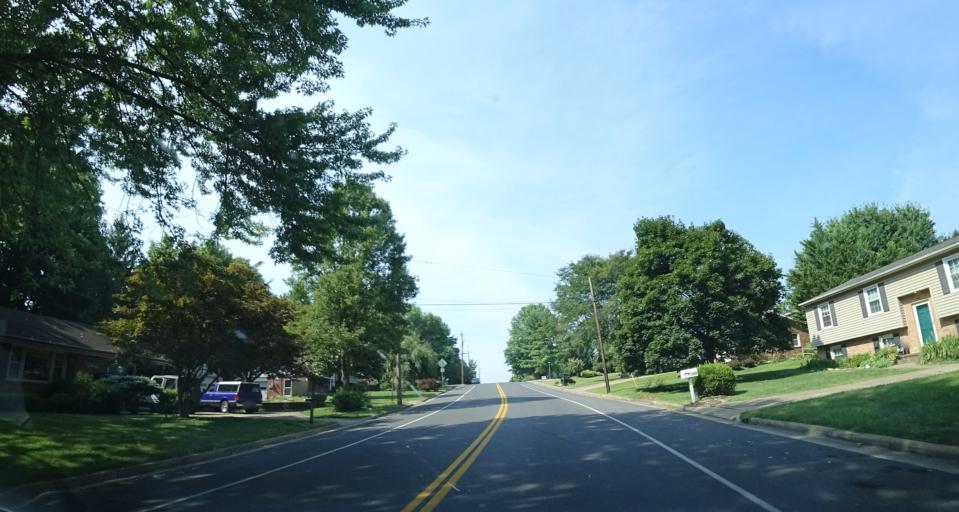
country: US
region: Virginia
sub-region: City of Harrisonburg
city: Harrisonburg
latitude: 38.4335
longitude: -78.8882
